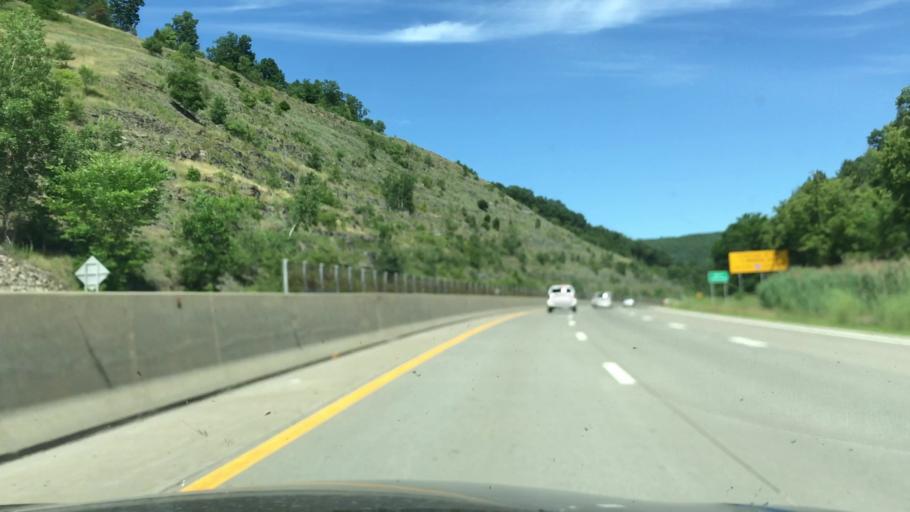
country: US
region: New York
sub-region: Steuben County
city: Corning
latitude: 42.1633
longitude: -77.0671
